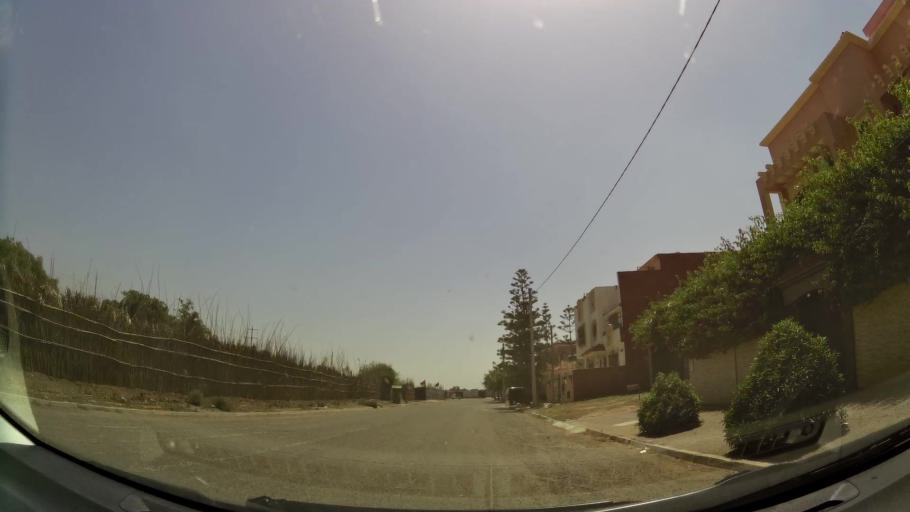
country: MA
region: Souss-Massa-Draa
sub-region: Inezgane-Ait Mellou
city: Inezgane
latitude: 30.3445
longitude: -9.4817
